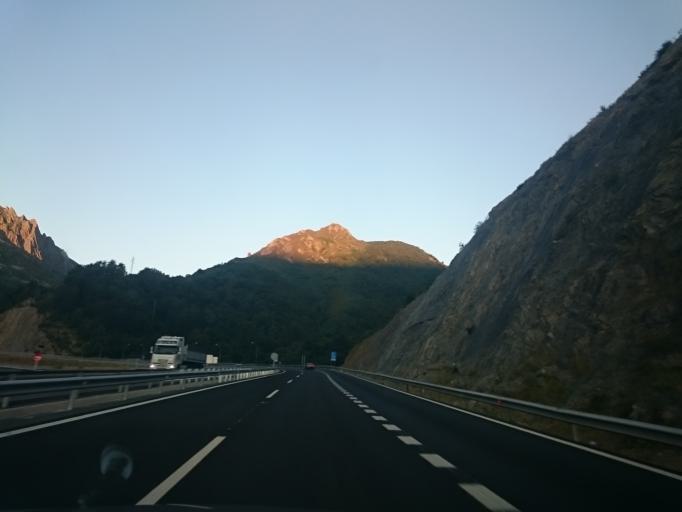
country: ES
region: Castille and Leon
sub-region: Provincia de Leon
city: Sena de Luna
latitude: 42.9836
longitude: -5.8284
